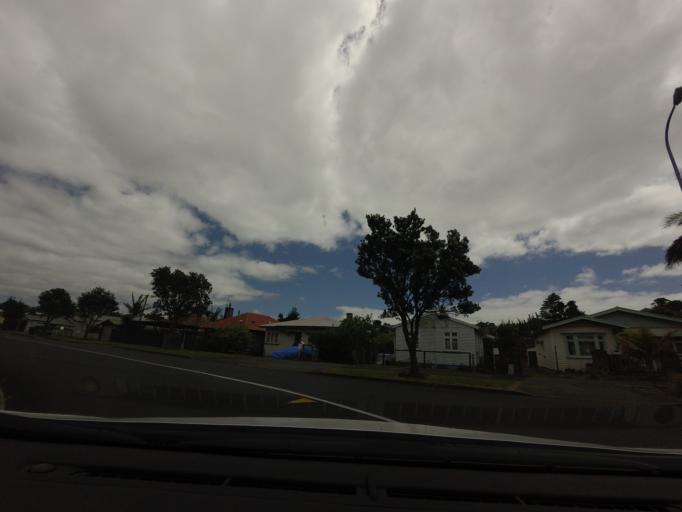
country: NZ
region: Auckland
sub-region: Auckland
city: Auckland
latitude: -36.8675
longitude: 174.7334
